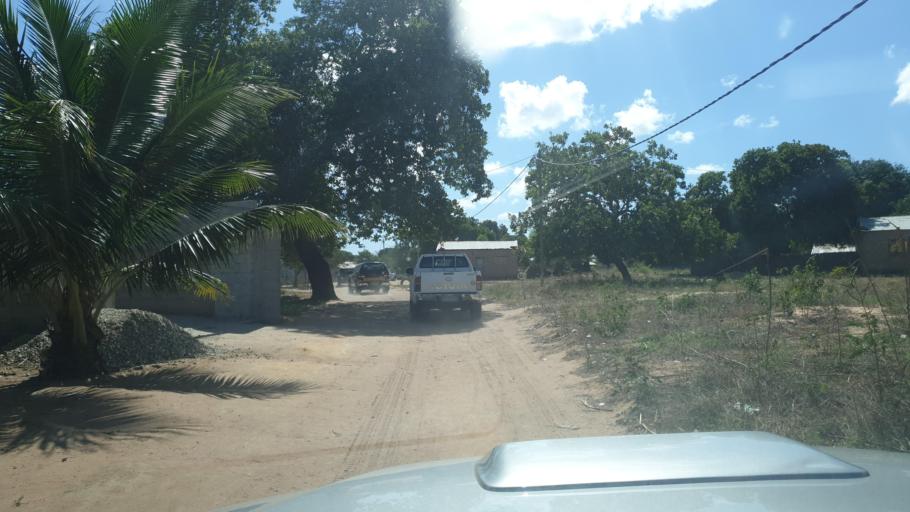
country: MZ
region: Nampula
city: Nacala
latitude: -14.4716
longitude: 40.6932
